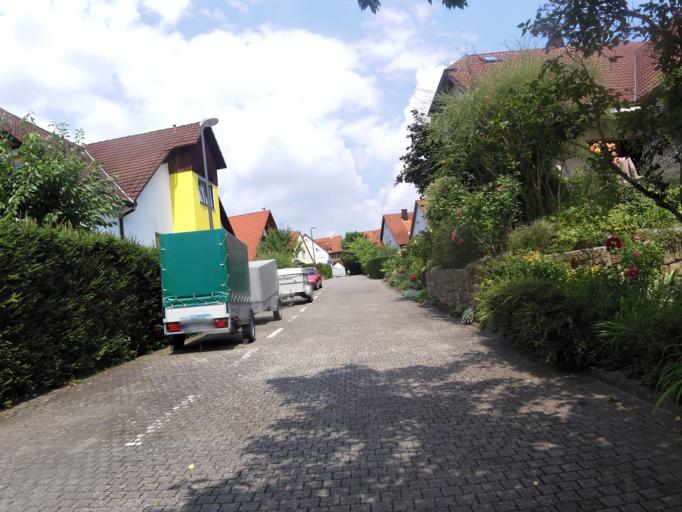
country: DE
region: Bavaria
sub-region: Regierungsbezirk Unterfranken
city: Randersacker
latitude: 49.7346
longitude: 9.9595
